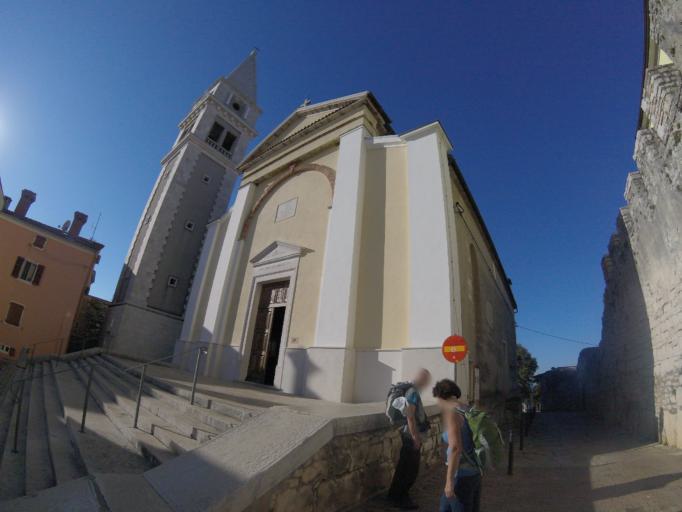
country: HR
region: Istarska
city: Vrsar
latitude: 45.1510
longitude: 13.6065
